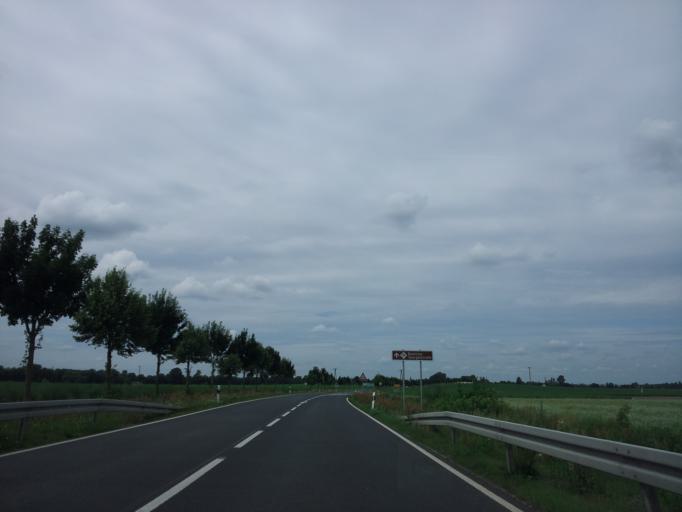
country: DE
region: Brandenburg
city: Beelitz
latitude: 52.2315
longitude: 13.0107
